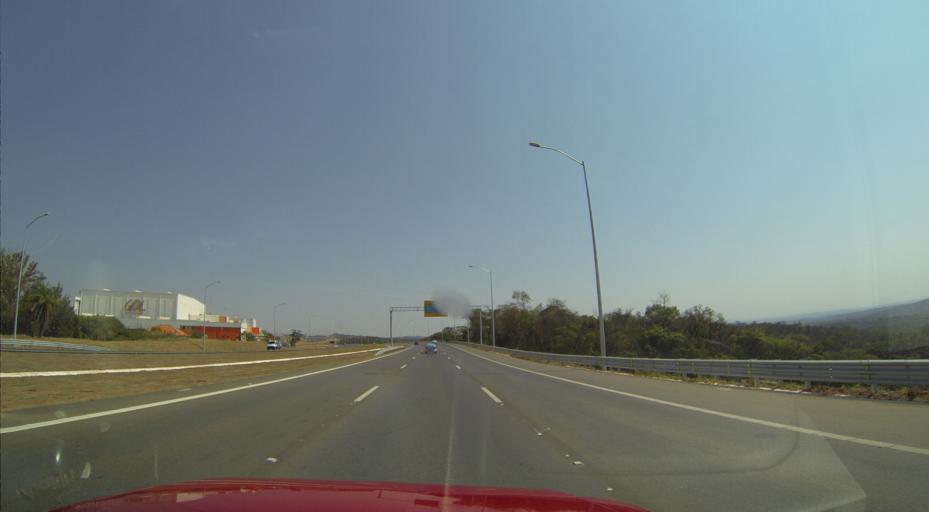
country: BR
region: Minas Gerais
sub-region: Lagoa Santa
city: Lagoa Santa
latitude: -19.6477
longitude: -43.9487
